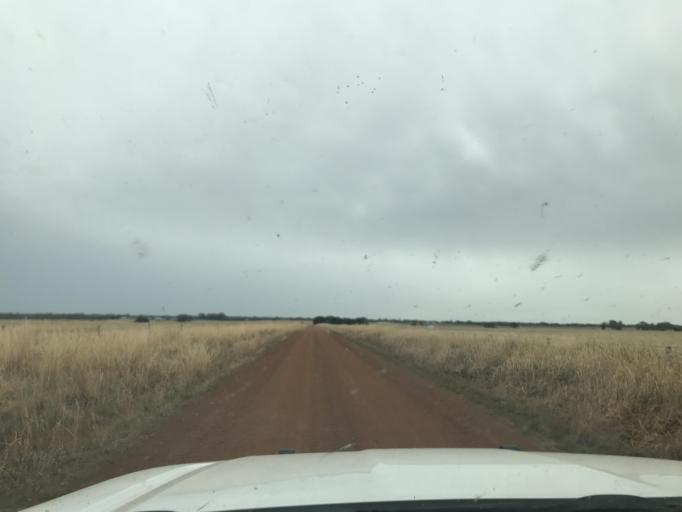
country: AU
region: Victoria
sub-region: Horsham
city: Horsham
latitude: -37.0602
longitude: 141.6069
